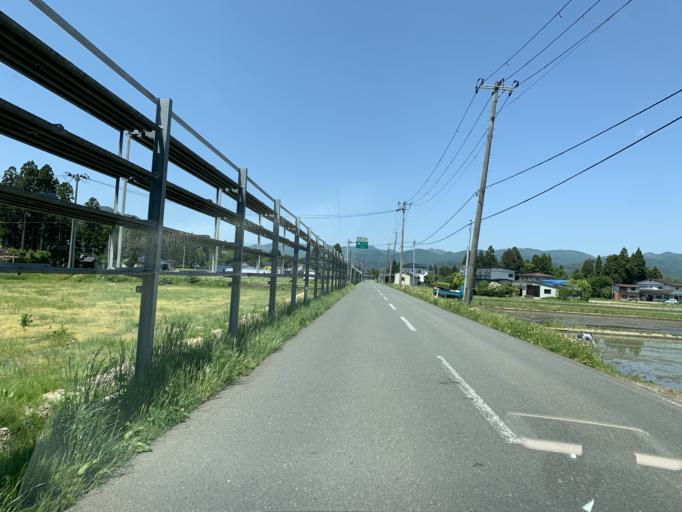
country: JP
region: Iwate
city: Kitakami
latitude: 39.2922
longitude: 140.9941
